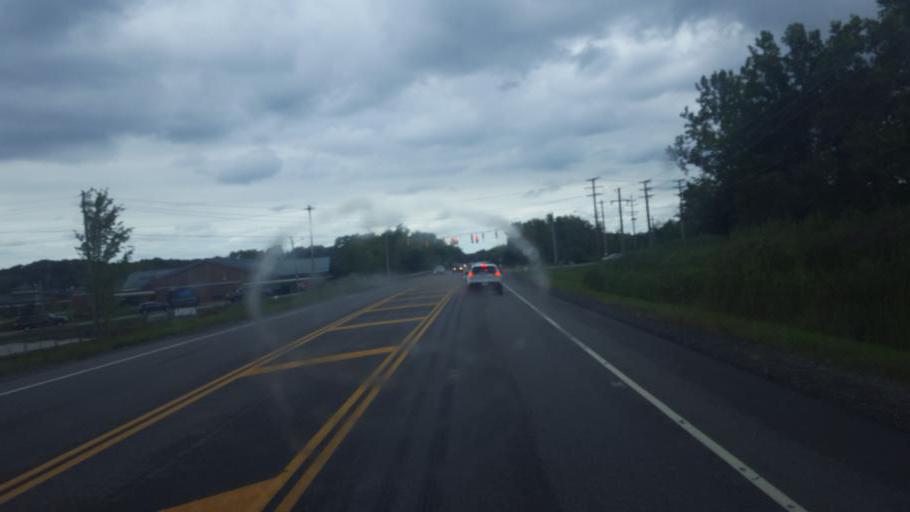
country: US
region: Ohio
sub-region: Lake County
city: Painesville
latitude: 41.6462
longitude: -81.2418
